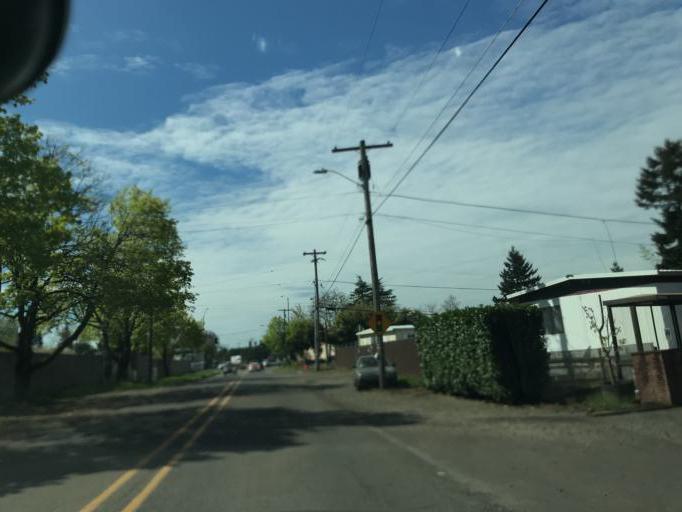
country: US
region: Oregon
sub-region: Multnomah County
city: Lents
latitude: 45.4581
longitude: -122.5744
